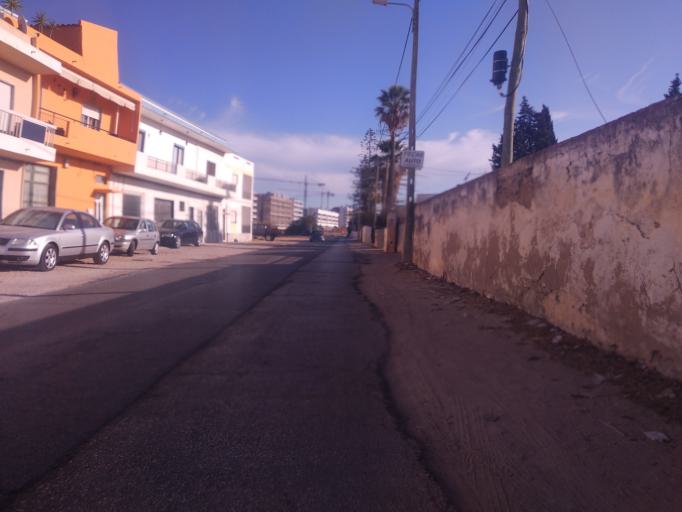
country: PT
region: Faro
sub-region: Faro
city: Faro
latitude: 37.0353
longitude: -7.9401
